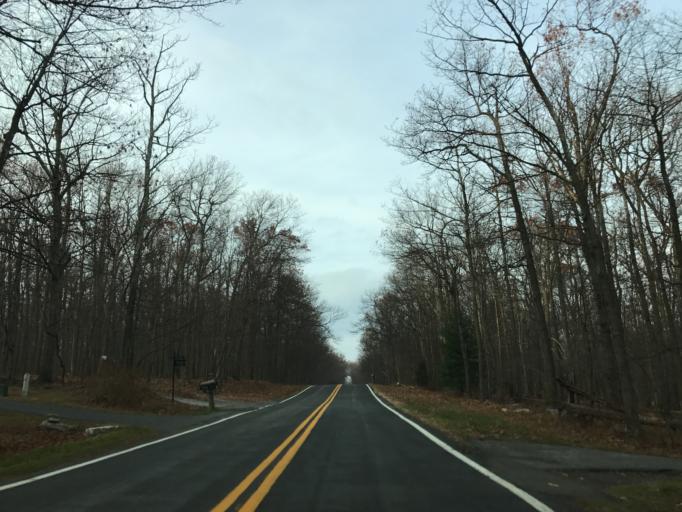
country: US
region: Maryland
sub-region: Frederick County
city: Myersville
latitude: 39.5321
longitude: -77.4972
